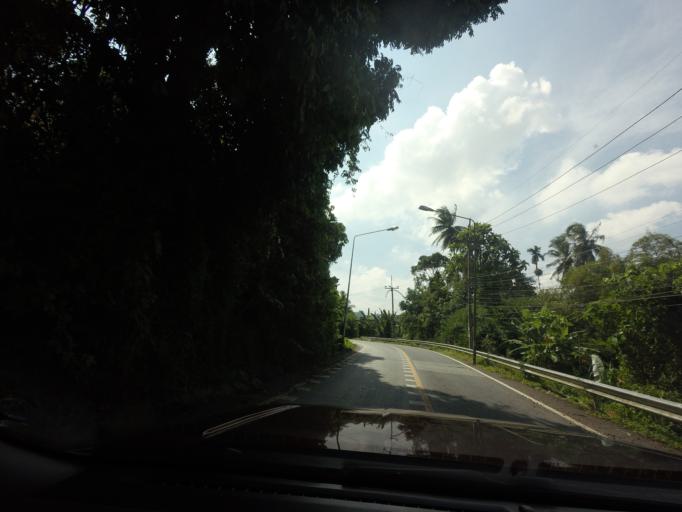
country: TH
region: Yala
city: Betong
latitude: 5.8057
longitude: 101.0721
